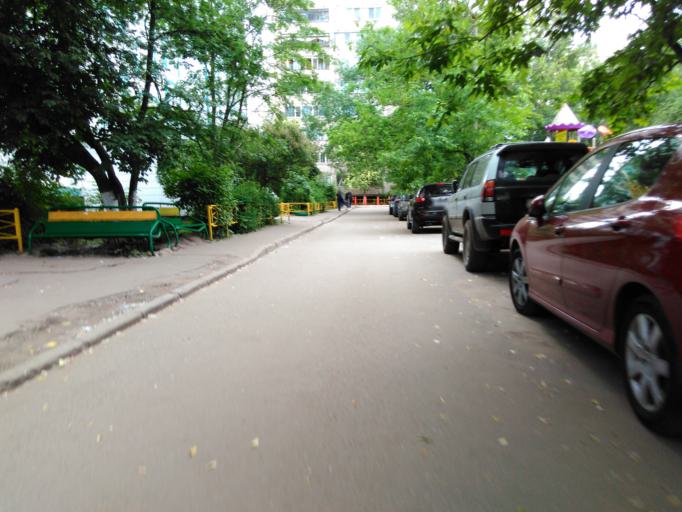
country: RU
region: Moskovskaya
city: Reutov
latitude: 55.7468
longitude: 37.8640
